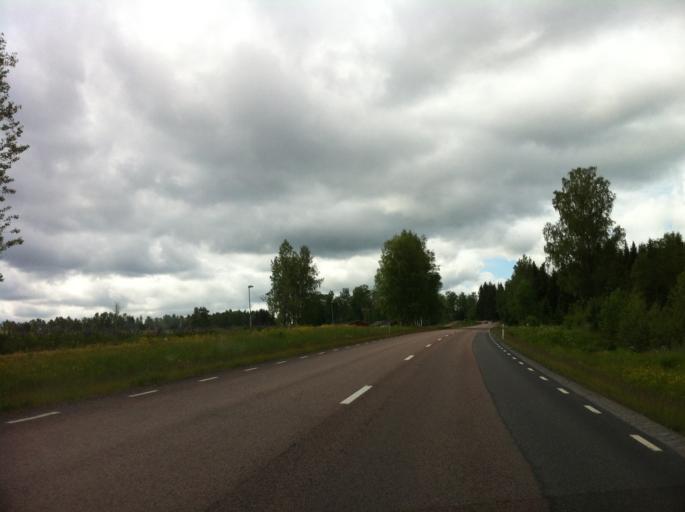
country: SE
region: Vaermland
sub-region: Sunne Kommun
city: Sunne
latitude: 59.8170
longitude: 13.1298
